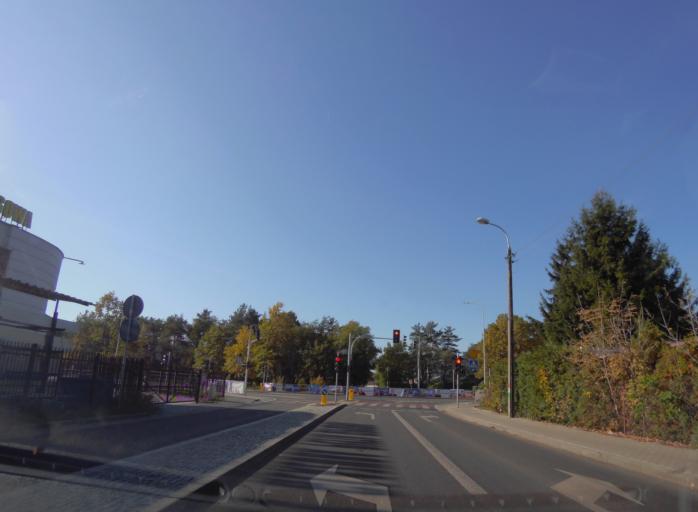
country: PL
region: Masovian Voivodeship
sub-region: Powiat otwocki
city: Jozefow
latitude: 52.1310
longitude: 21.2432
